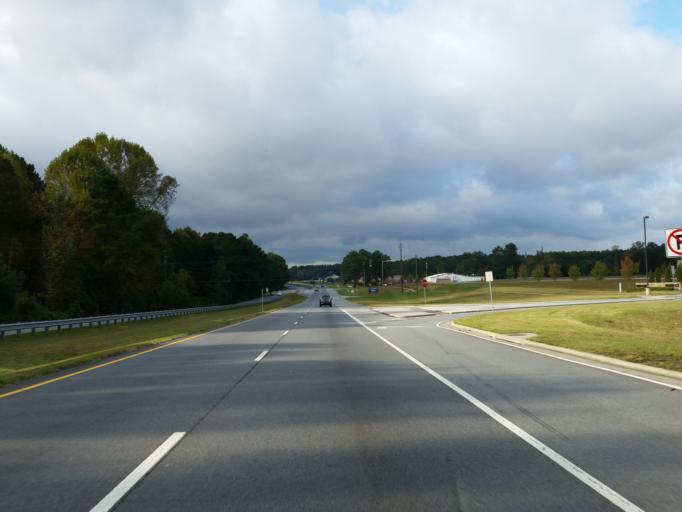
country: US
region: Georgia
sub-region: Cobb County
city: Acworth
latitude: 34.0668
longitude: -84.7246
